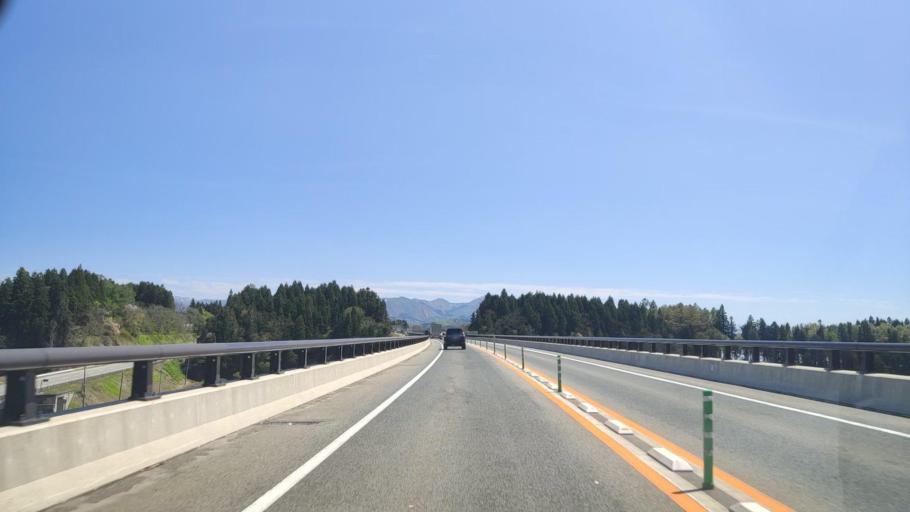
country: JP
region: Yamagata
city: Obanazawa
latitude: 38.6308
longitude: 140.3736
